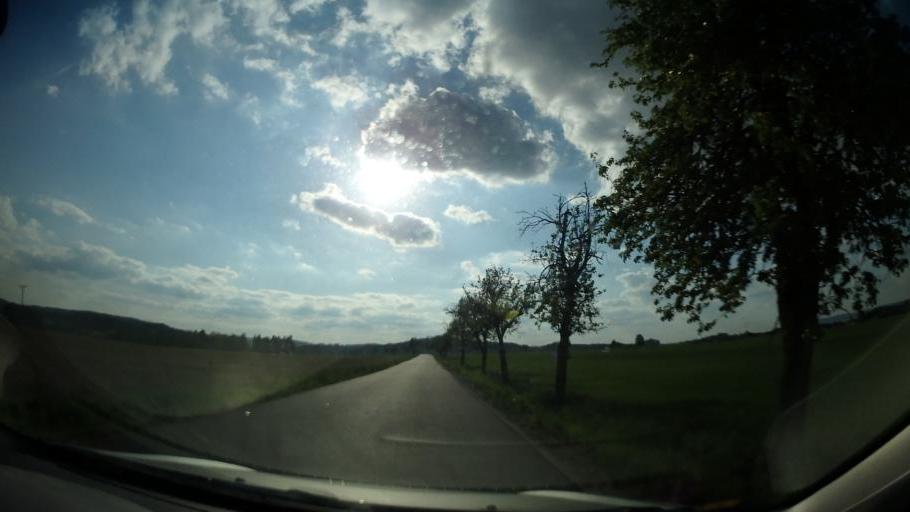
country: CZ
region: Vysocina
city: Merin
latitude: 49.3554
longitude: 15.9122
